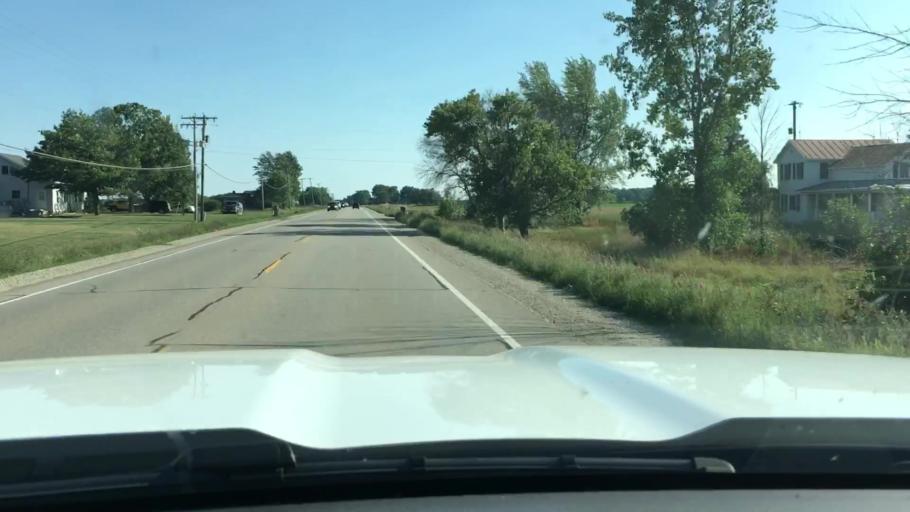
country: US
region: Michigan
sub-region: Ottawa County
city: Coopersville
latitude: 43.0370
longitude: -85.9567
